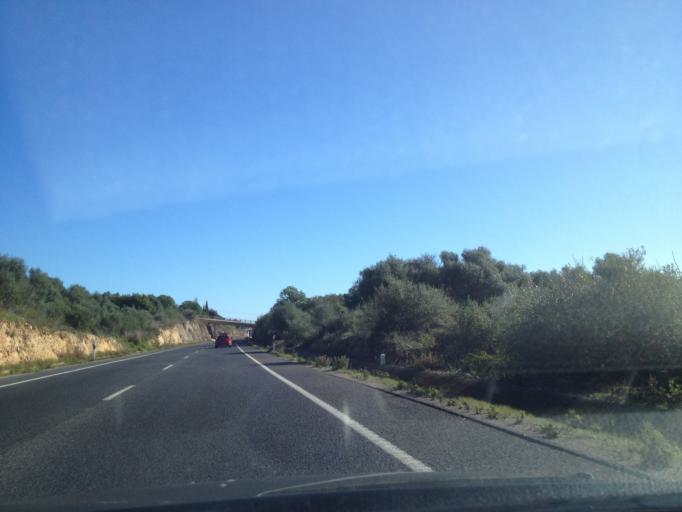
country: ES
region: Balearic Islands
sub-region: Illes Balears
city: Manacor
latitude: 39.5864
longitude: 3.2215
